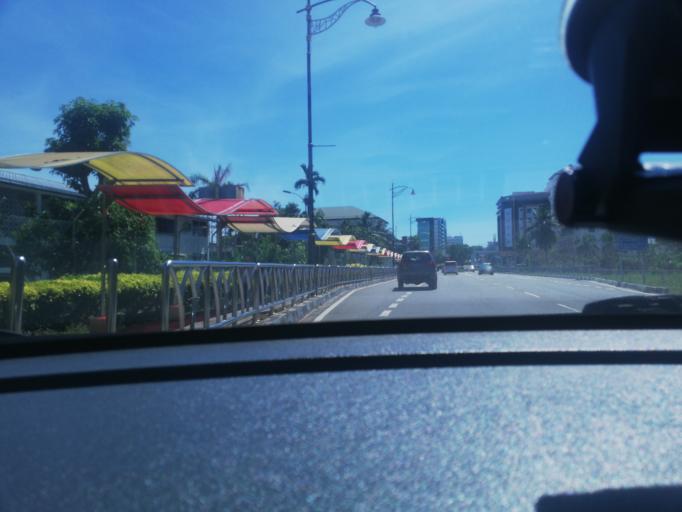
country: MY
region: Labuan
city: Victoria
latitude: 5.2773
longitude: 115.2480
